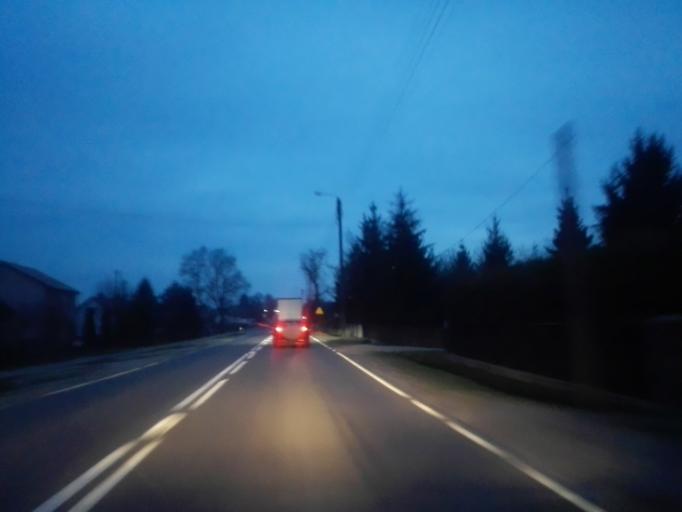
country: PL
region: Podlasie
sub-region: Lomza
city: Lomza
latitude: 53.1287
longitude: 22.0391
